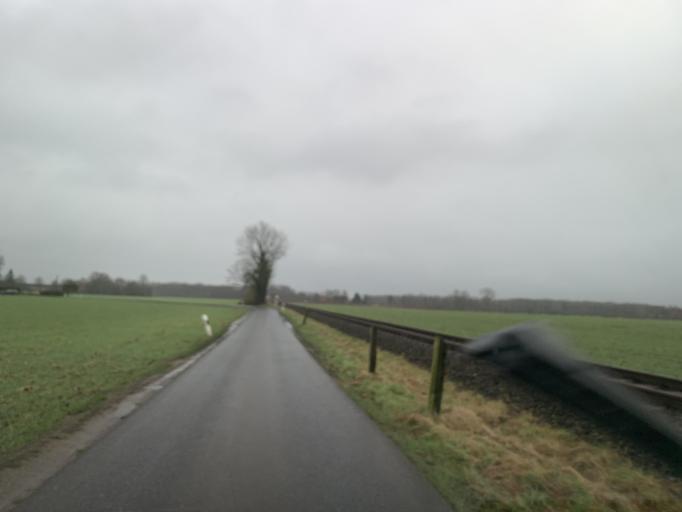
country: DE
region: North Rhine-Westphalia
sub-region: Regierungsbezirk Munster
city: Muenster
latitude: 51.9372
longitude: 7.5405
